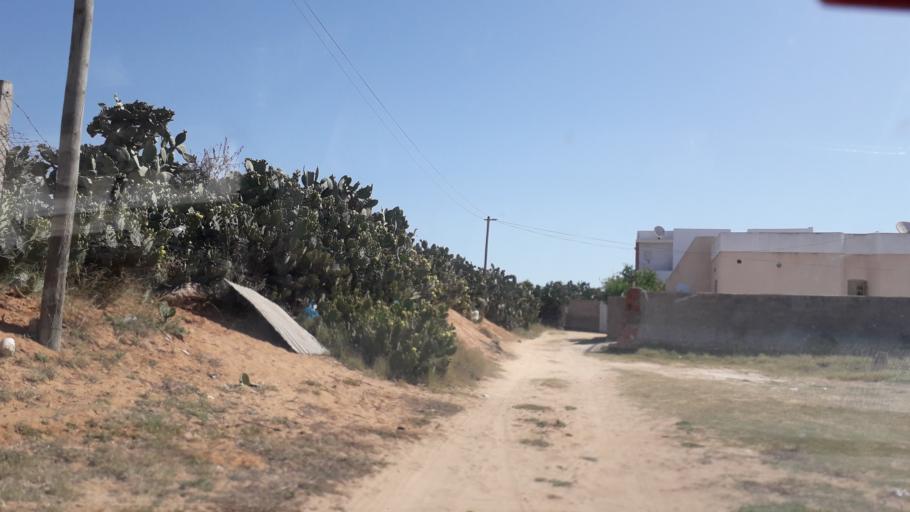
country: TN
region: Safaqis
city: Al Qarmadah
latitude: 34.8096
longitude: 10.7680
